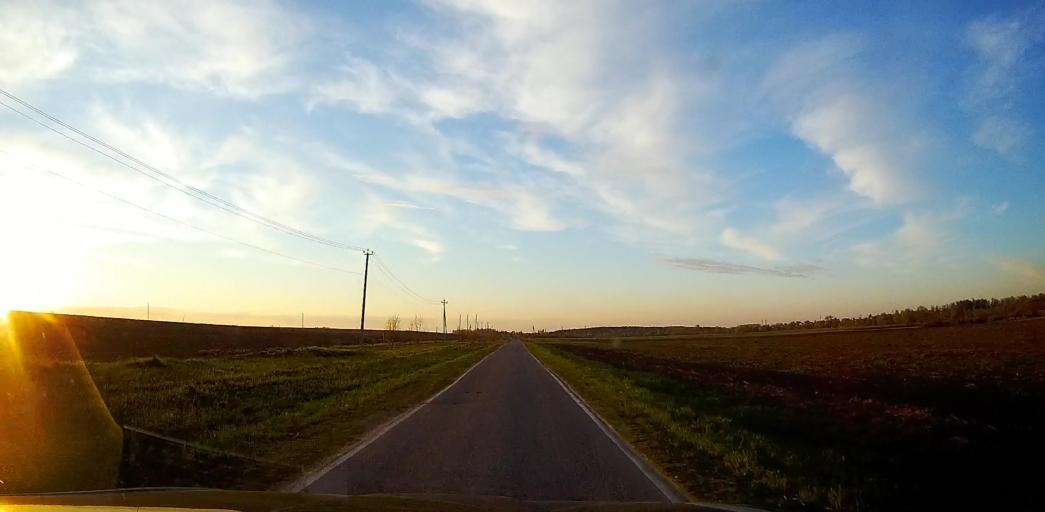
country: RU
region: Moskovskaya
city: Peski
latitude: 55.2157
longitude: 38.7388
